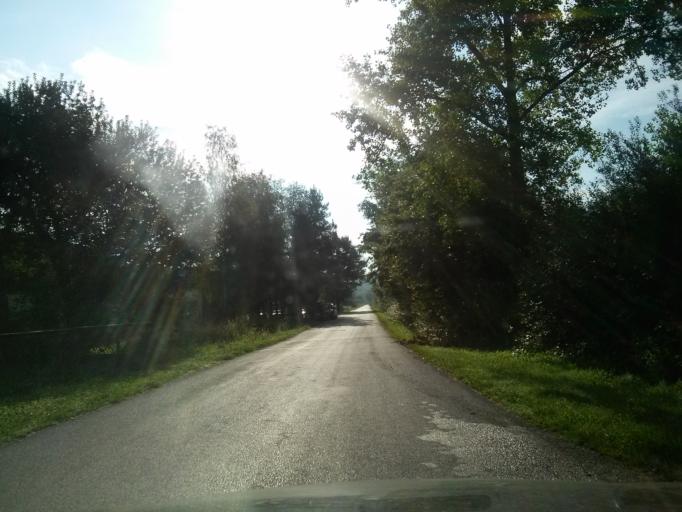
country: HR
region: Sisacko-Moslavacka
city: Gvozd
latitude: 45.2957
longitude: 15.9799
